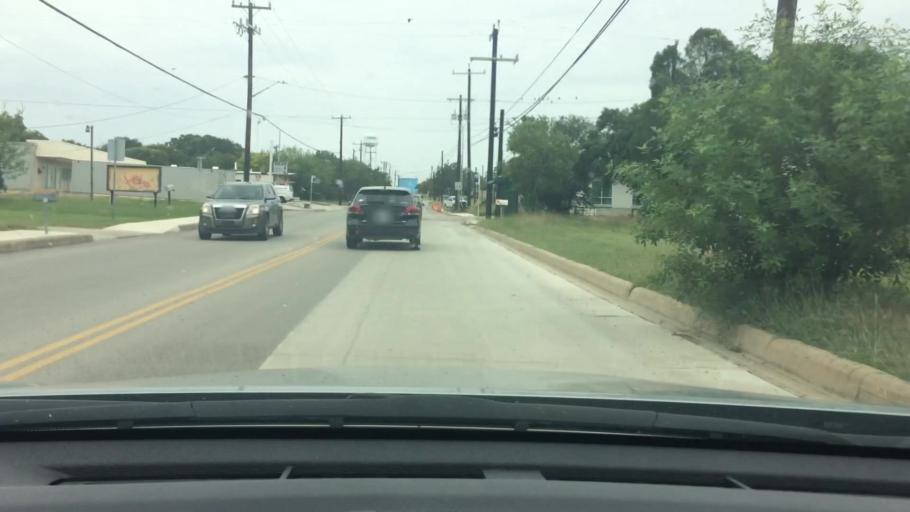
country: US
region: Texas
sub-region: Bexar County
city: Converse
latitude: 29.5218
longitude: -98.3191
